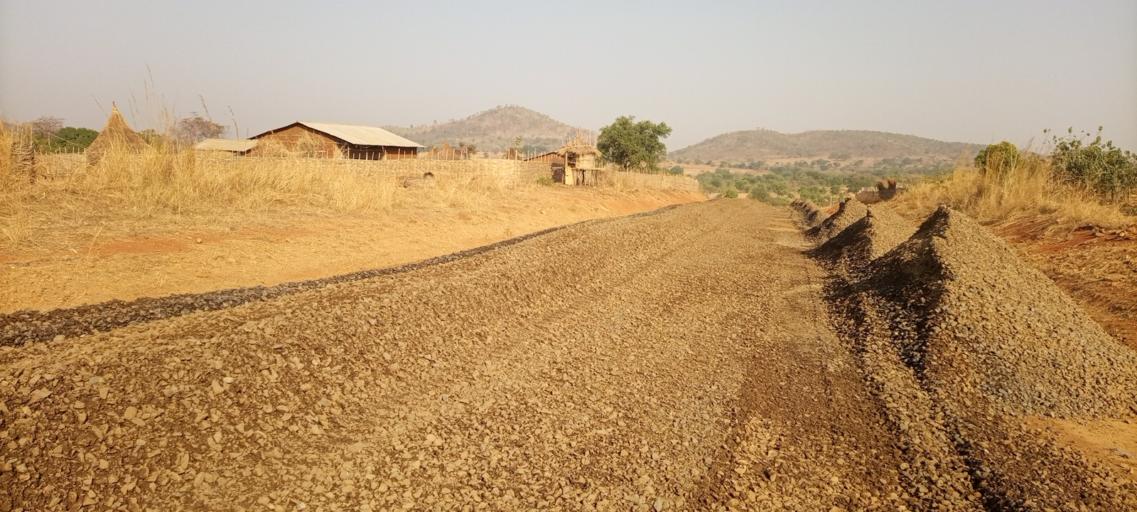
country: ET
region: Oromiya
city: Mendi
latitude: 10.2041
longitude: 35.0911
